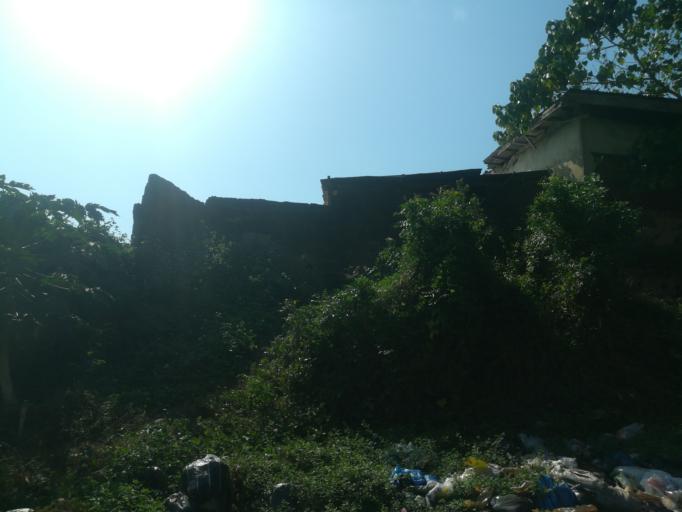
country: NG
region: Ogun
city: Abeokuta
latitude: 7.1502
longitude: 3.3390
